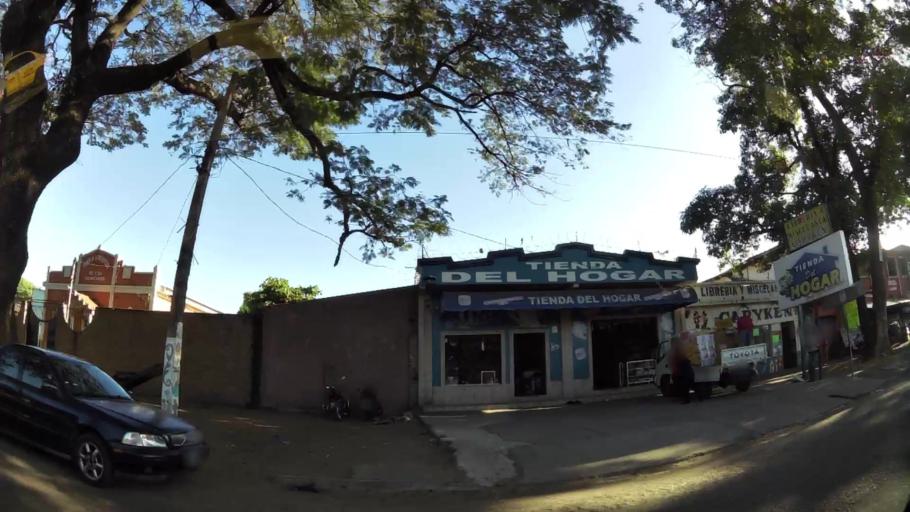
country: SV
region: Sonsonate
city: Sonsonate
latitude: 13.7160
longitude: -89.7211
